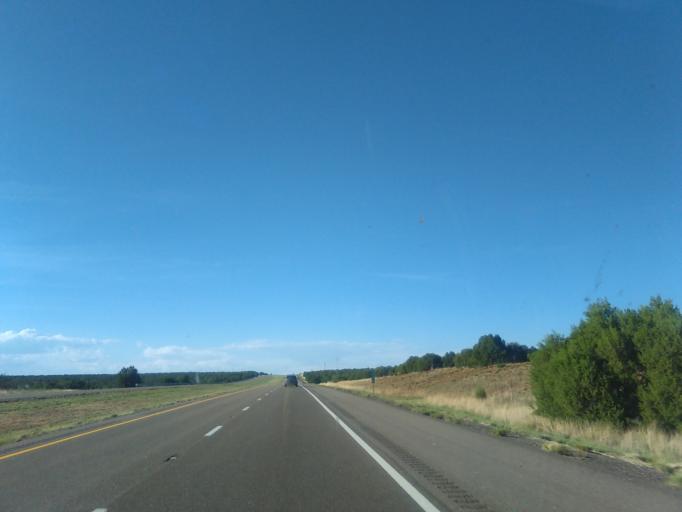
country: US
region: New Mexico
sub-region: San Miguel County
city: Las Vegas
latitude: 35.4676
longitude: -105.2759
